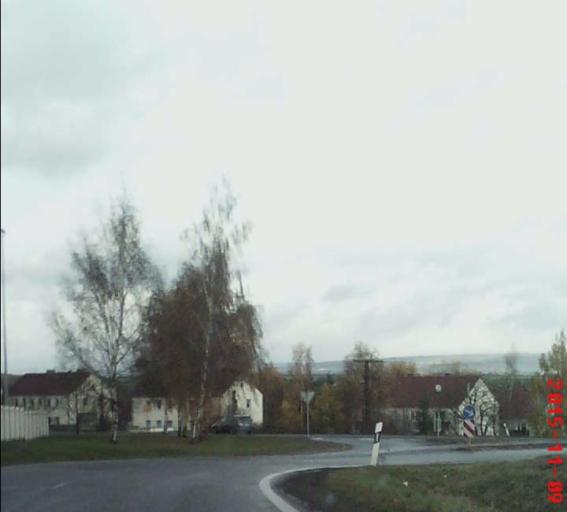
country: DE
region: Thuringia
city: Seebach
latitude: 51.1774
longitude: 10.5081
